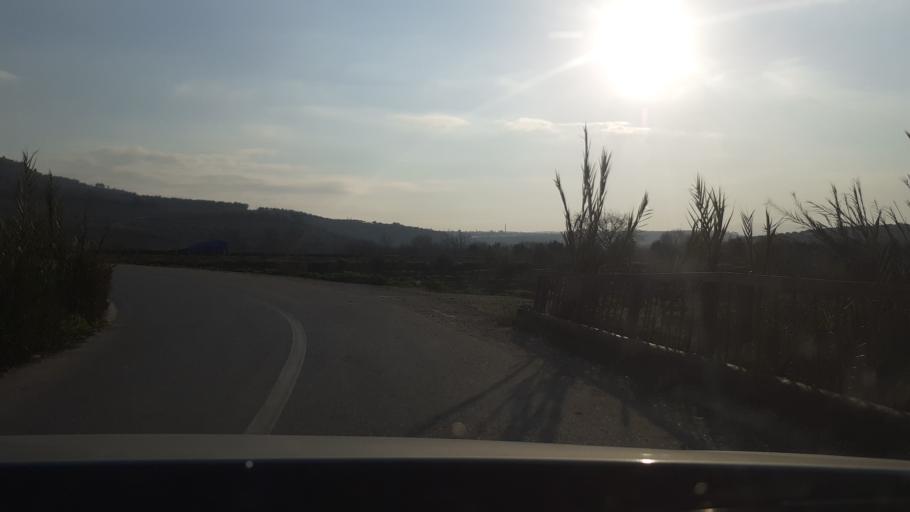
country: TR
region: Hatay
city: Oymakli
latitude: 36.1281
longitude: 36.3096
